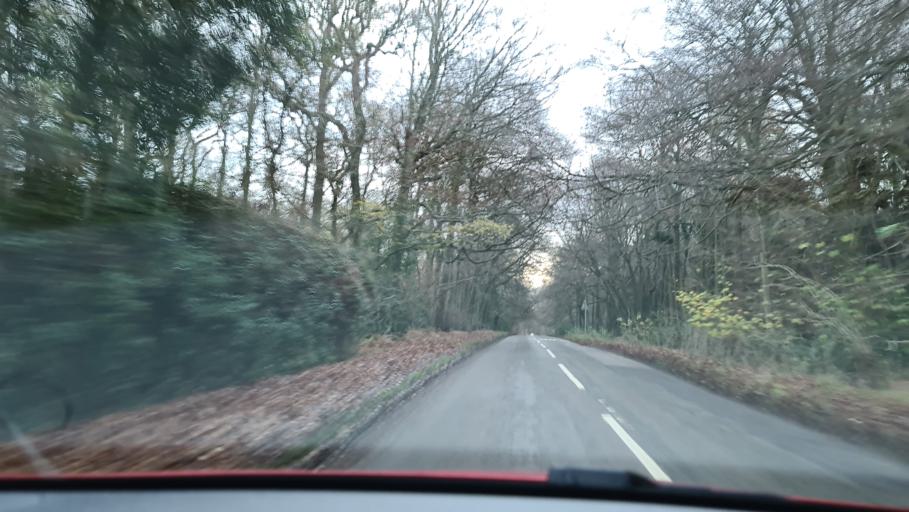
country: GB
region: England
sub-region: Buckinghamshire
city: Princes Risborough
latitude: 51.7097
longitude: -0.8019
